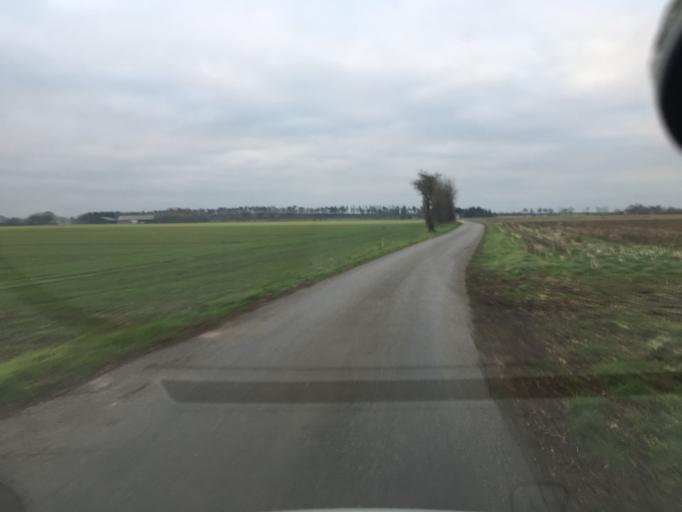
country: DK
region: South Denmark
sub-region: Tonder Kommune
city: Logumkloster
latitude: 55.0594
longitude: 9.0663
